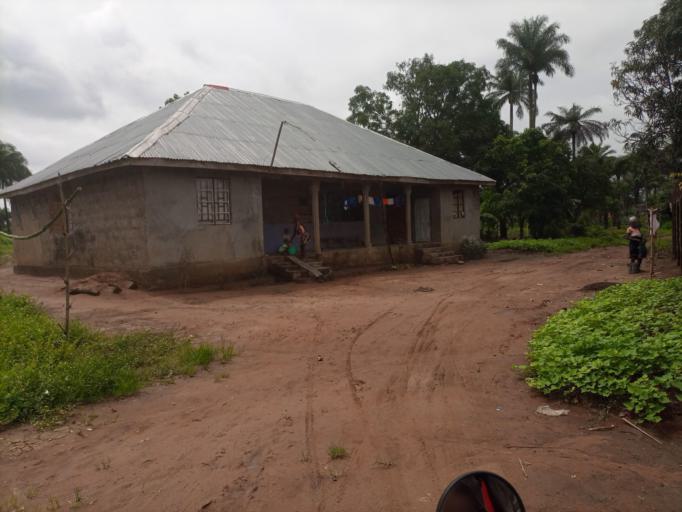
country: SL
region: Northern Province
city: Sawkta
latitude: 8.6473
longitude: -13.1902
